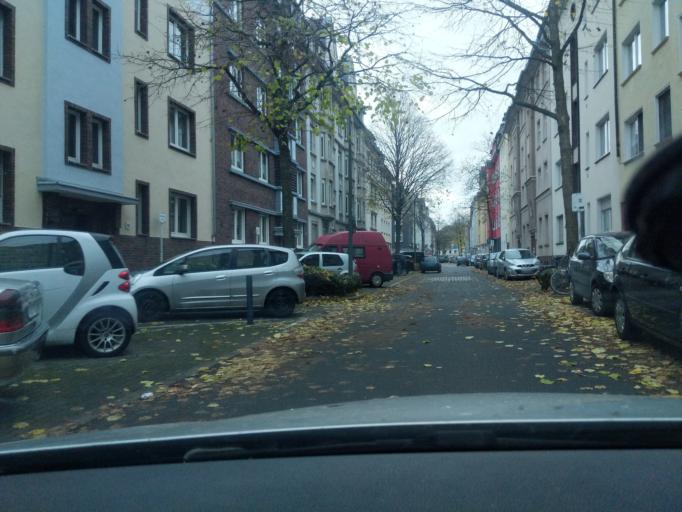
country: DE
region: North Rhine-Westphalia
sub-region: Regierungsbezirk Arnsberg
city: Dortmund
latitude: 51.5043
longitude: 7.4500
